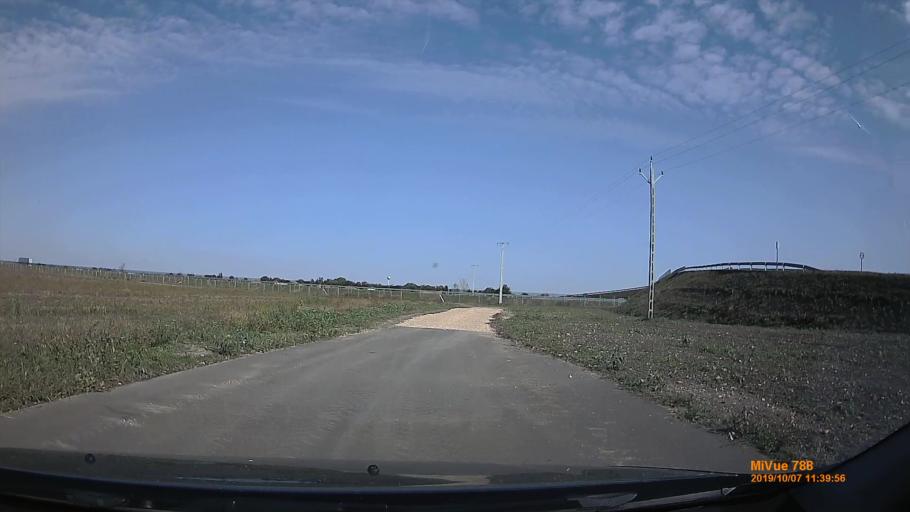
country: HU
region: Bekes
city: Kondoros
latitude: 46.7868
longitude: 20.7096
